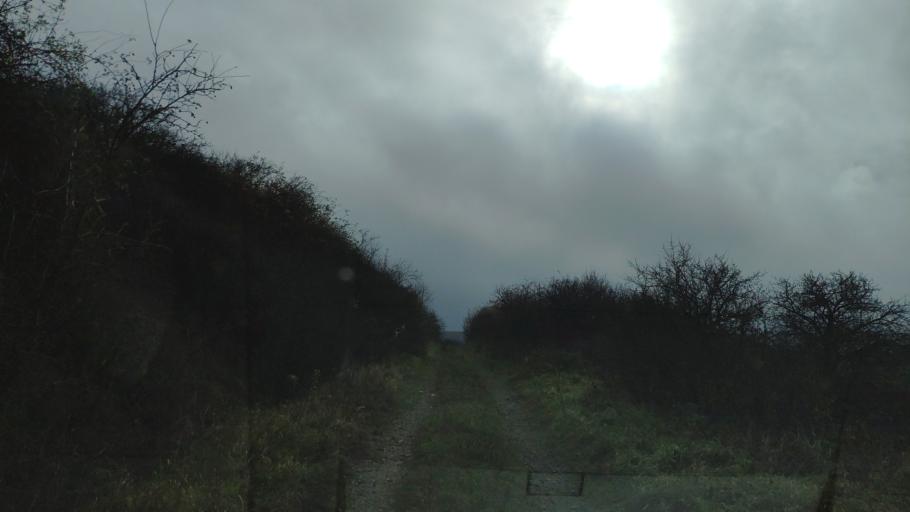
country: SK
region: Presovsky
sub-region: Okres Presov
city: Presov
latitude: 49.0201
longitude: 21.2001
